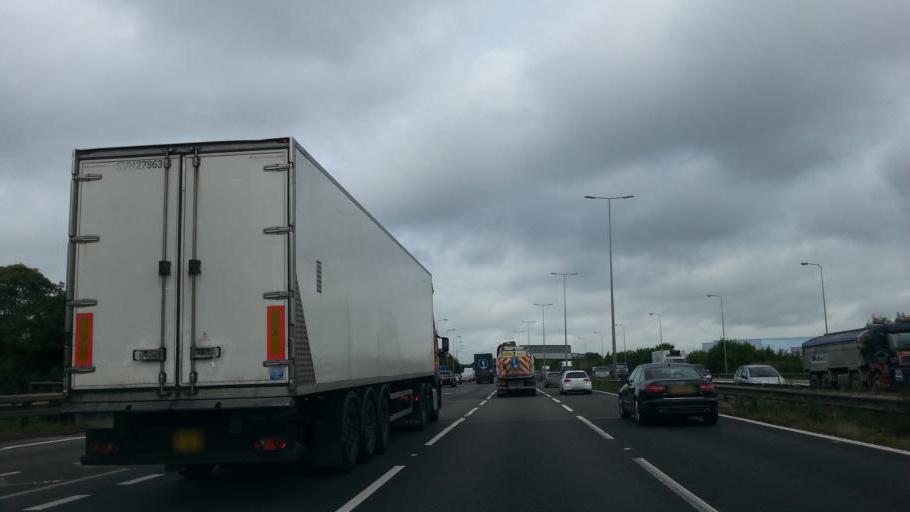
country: GB
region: England
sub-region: Leicestershire
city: Enderby
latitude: 52.6050
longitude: -1.1963
